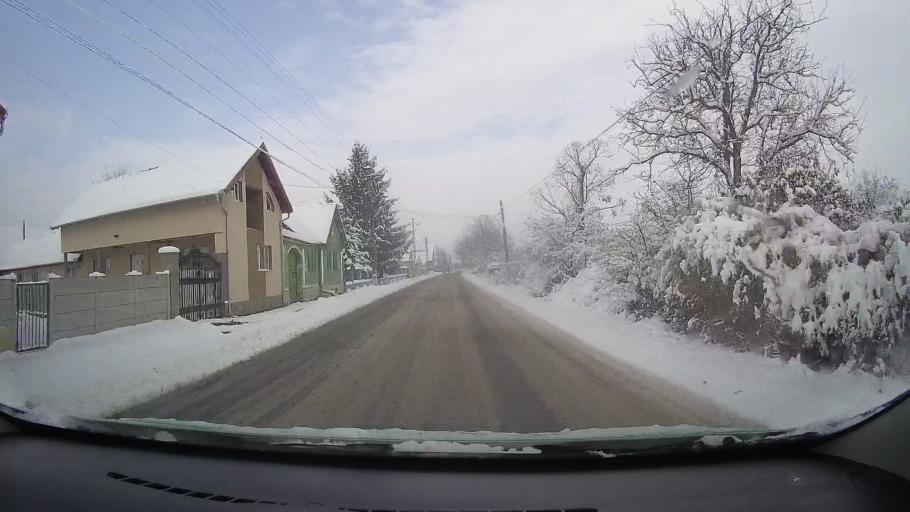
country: RO
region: Alba
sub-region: Comuna Pianu
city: Pianu de Jos
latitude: 45.9413
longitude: 23.4837
